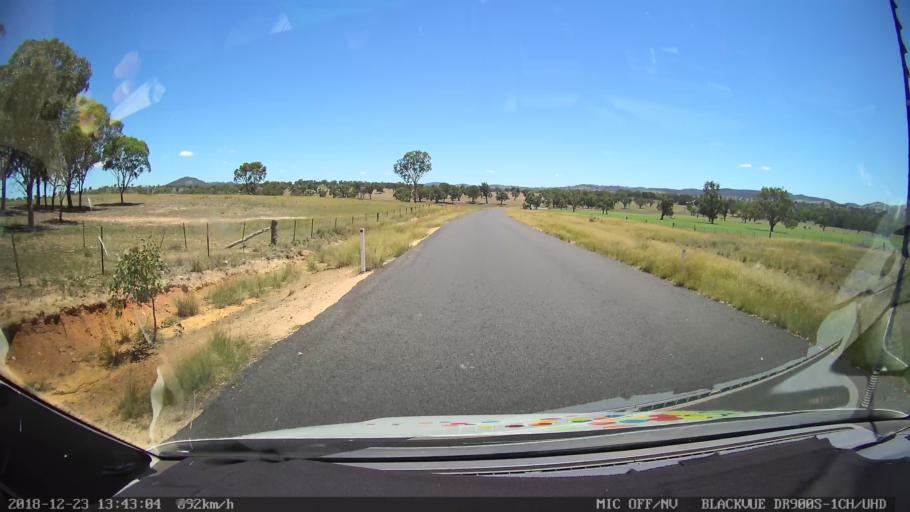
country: AU
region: New South Wales
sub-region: Tamworth Municipality
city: Manilla
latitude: -30.4832
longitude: 151.1554
